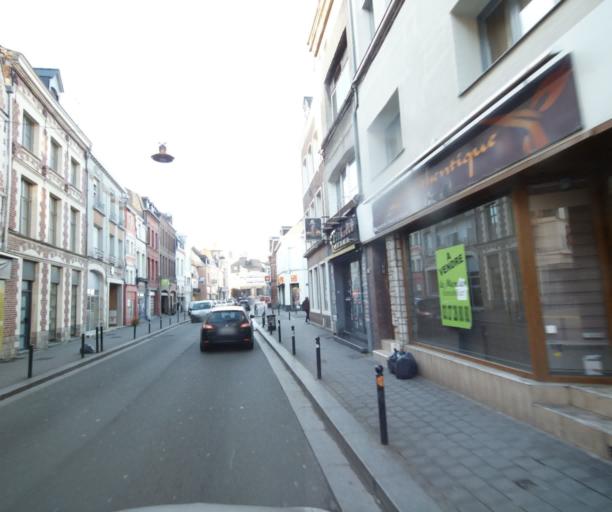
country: FR
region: Nord-Pas-de-Calais
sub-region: Departement du Nord
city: Valenciennes
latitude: 50.3616
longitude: 3.5223
